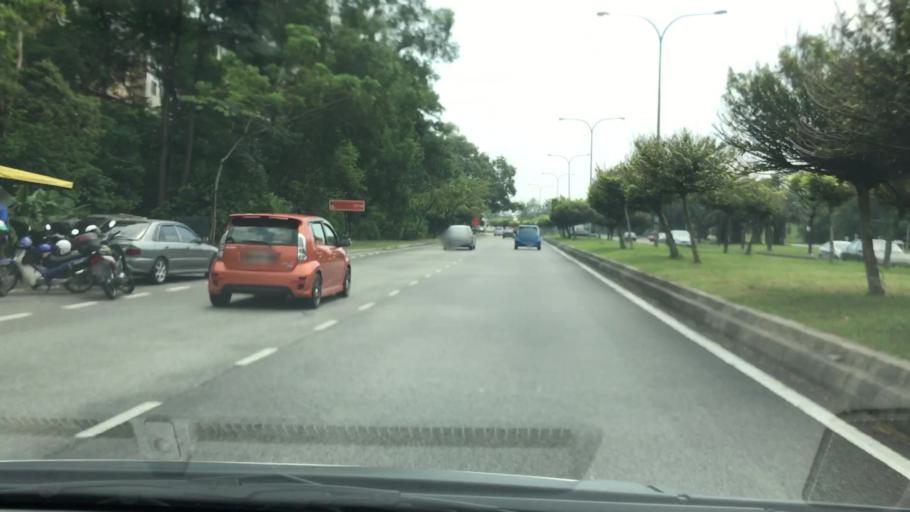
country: MY
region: Putrajaya
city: Putrajaya
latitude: 2.9951
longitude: 101.6640
